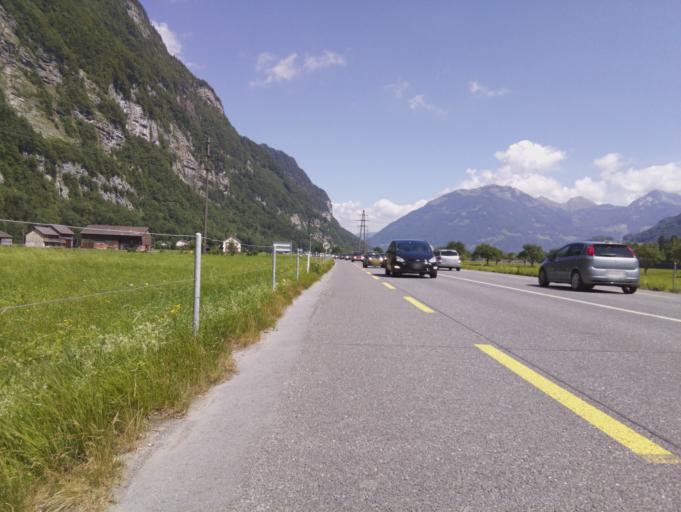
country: CH
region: Glarus
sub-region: Glarus
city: Netstal
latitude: 47.0738
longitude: 9.0562
